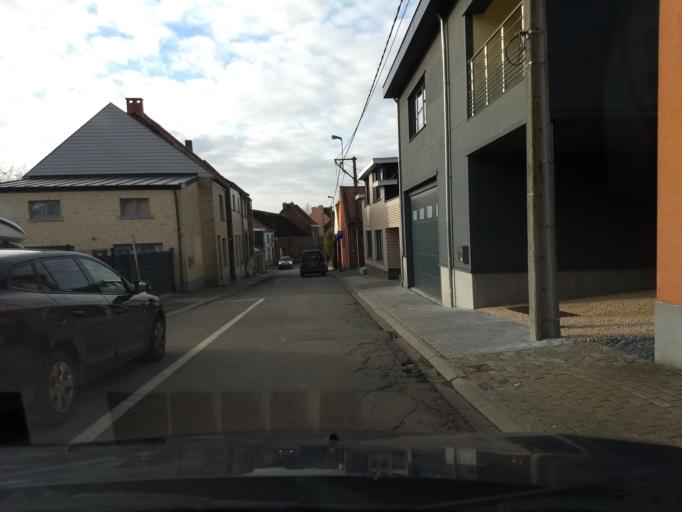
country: BE
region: Flanders
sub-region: Provincie Vlaams-Brabant
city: Halle
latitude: 50.7081
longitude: 4.2442
